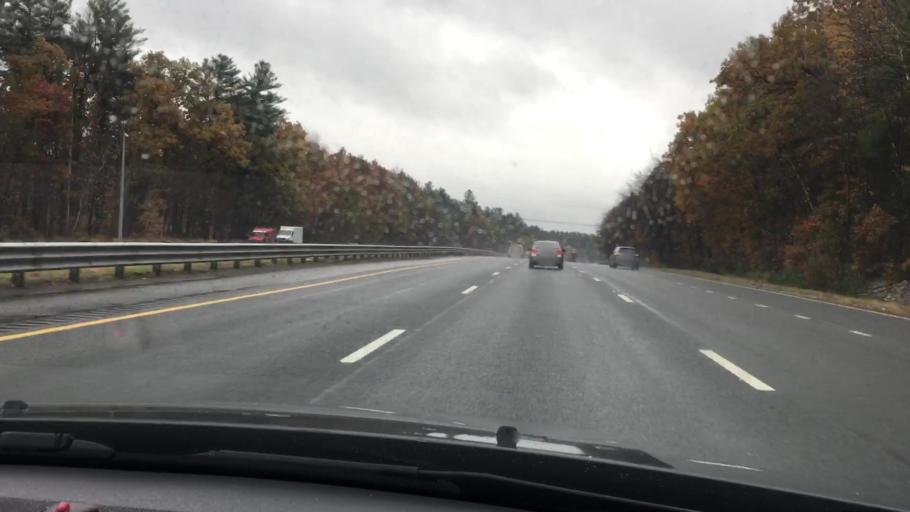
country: US
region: Massachusetts
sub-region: Middlesex County
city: Tyngsboro
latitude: 42.6915
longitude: -71.4449
